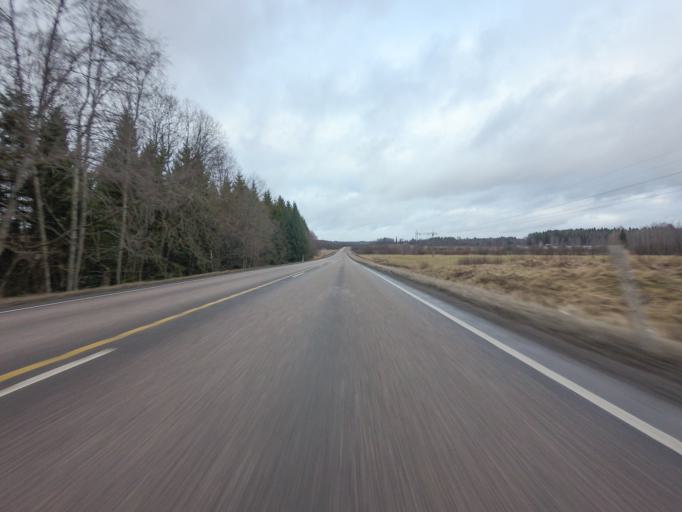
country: FI
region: Uusimaa
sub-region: Helsinki
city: Lohja
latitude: 60.1885
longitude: 24.0091
